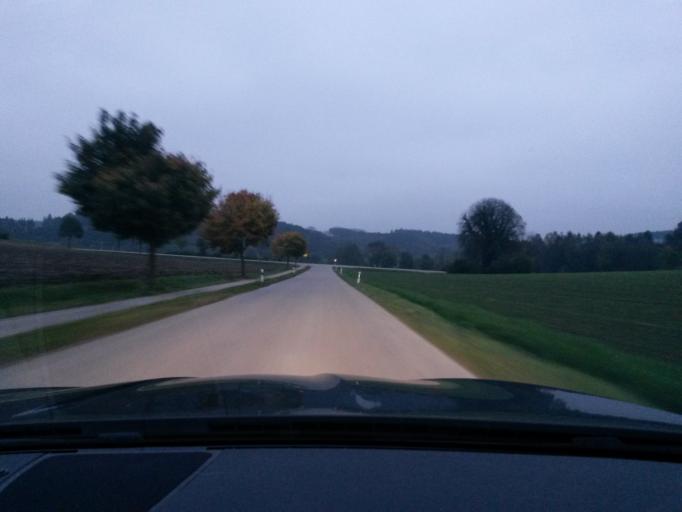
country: DE
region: Bavaria
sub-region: Lower Bavaria
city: Eching
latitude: 48.4904
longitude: 12.0556
